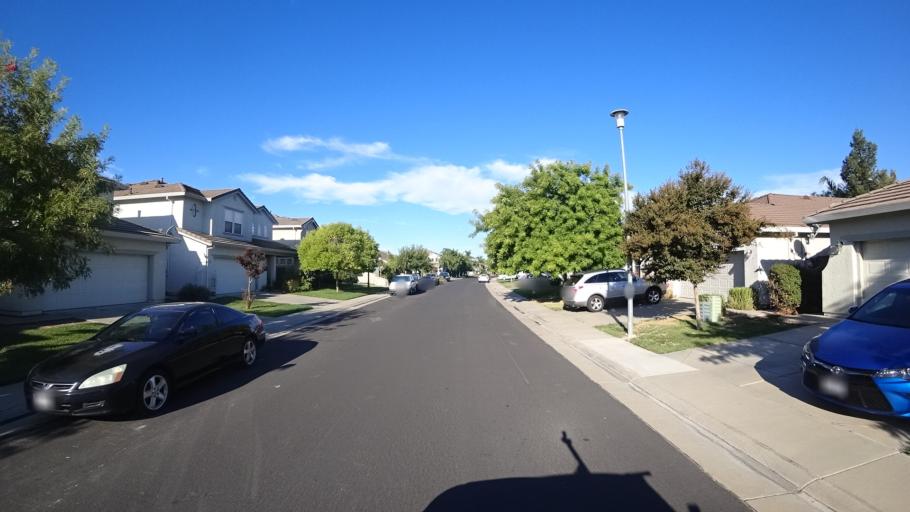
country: US
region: California
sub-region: Sacramento County
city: Laguna
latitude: 38.4040
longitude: -121.4687
